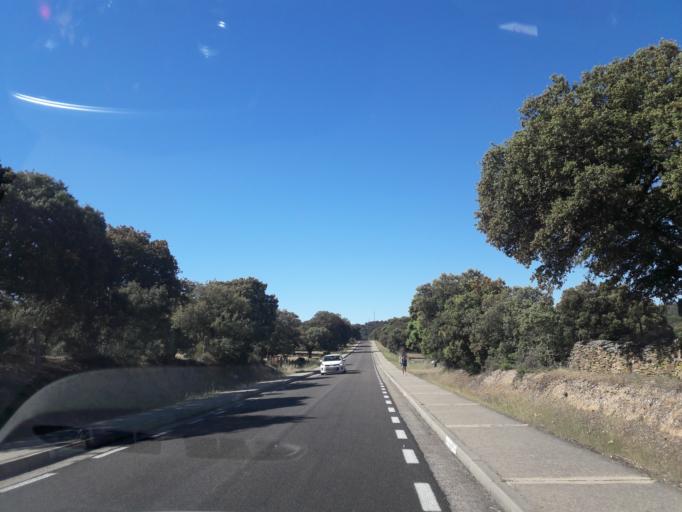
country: ES
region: Castille and Leon
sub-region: Provincia de Salamanca
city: Juzbado
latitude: 41.0806
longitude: -5.8970
